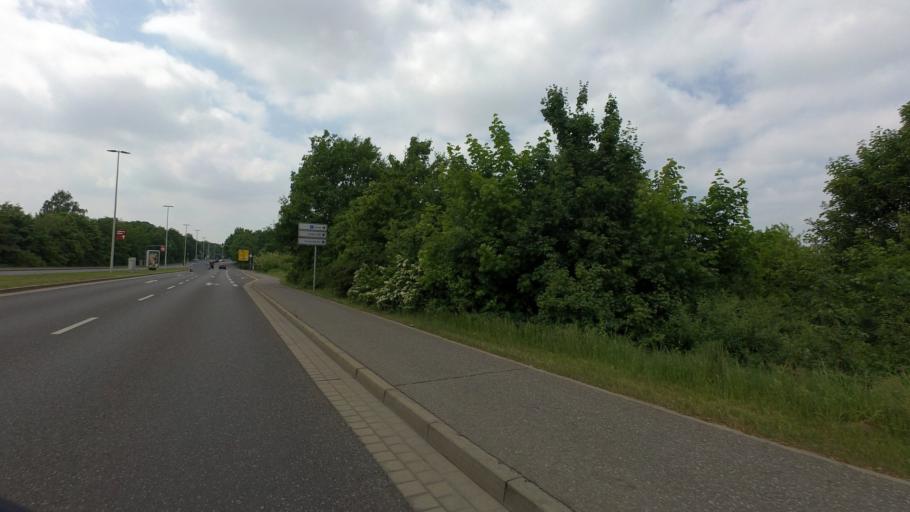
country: DE
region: Brandenburg
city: Cottbus
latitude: 51.7548
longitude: 14.3556
